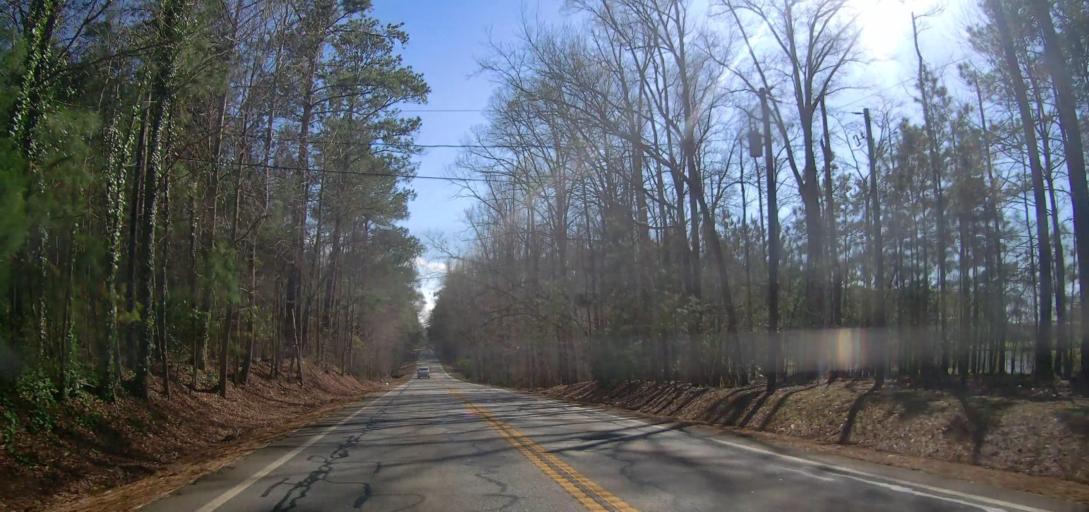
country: US
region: Georgia
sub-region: Butts County
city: Indian Springs
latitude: 33.2218
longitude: -83.9291
